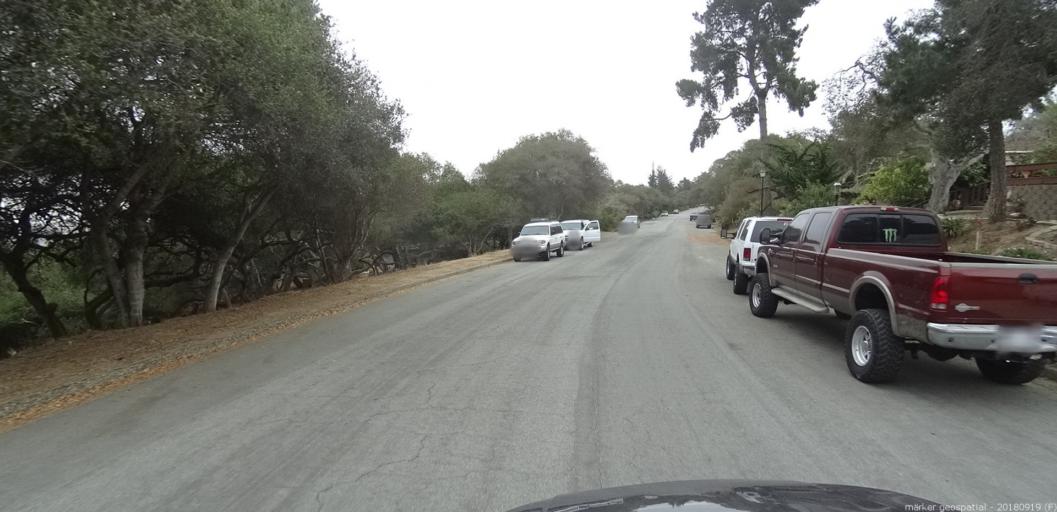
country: US
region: California
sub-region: Monterey County
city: Prunedale
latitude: 36.7824
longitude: -121.7110
